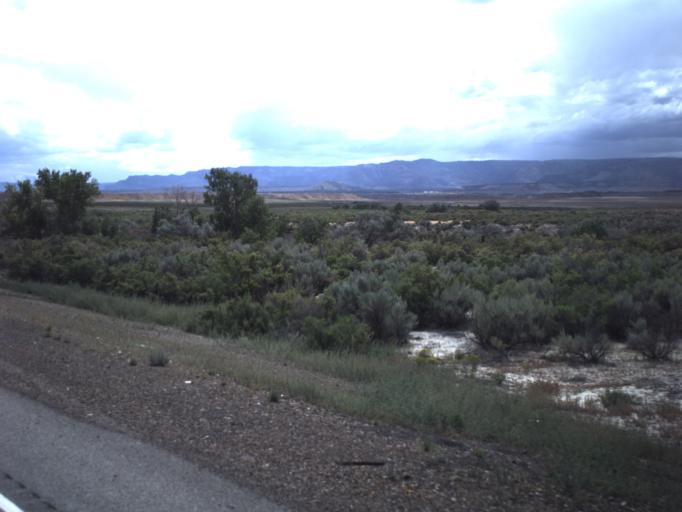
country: US
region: Utah
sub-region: Carbon County
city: Price
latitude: 39.5245
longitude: -110.8234
